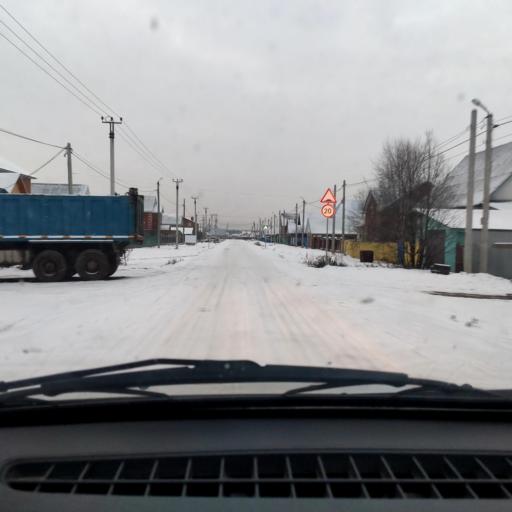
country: RU
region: Bashkortostan
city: Mikhaylovka
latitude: 54.7908
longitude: 55.8275
